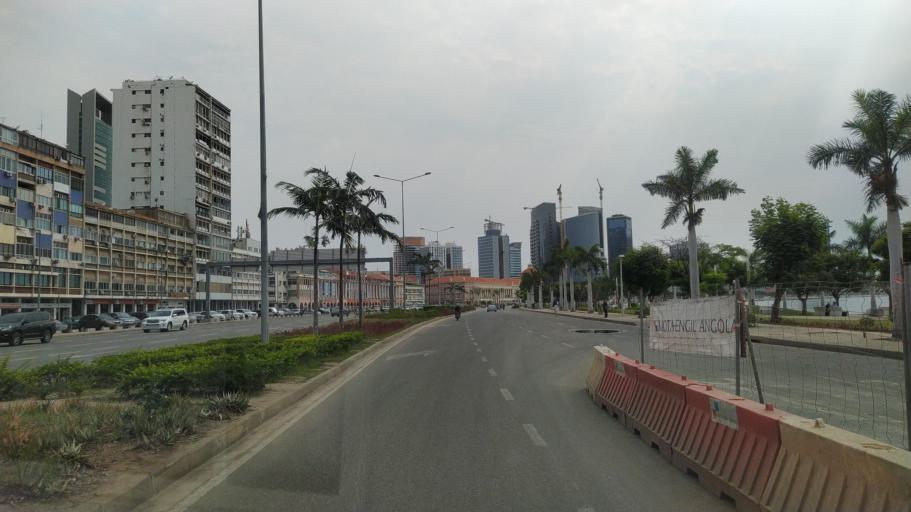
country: AO
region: Luanda
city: Luanda
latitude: -8.8074
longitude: 13.2383
